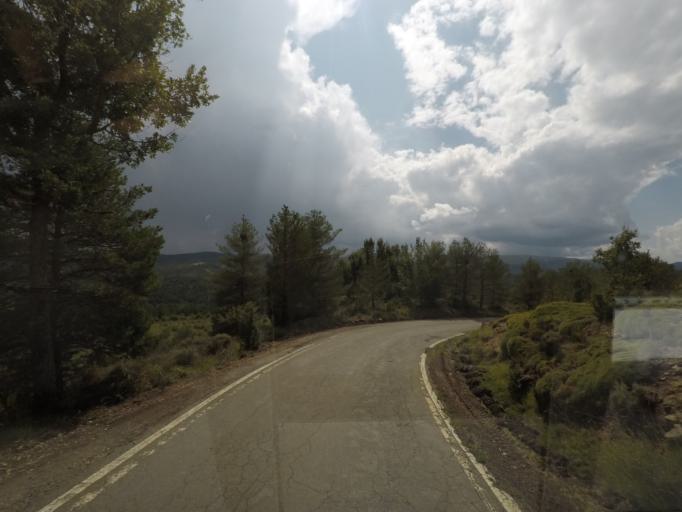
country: ES
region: Aragon
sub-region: Provincia de Huesca
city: Fiscal
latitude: 42.4111
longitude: -0.1293
